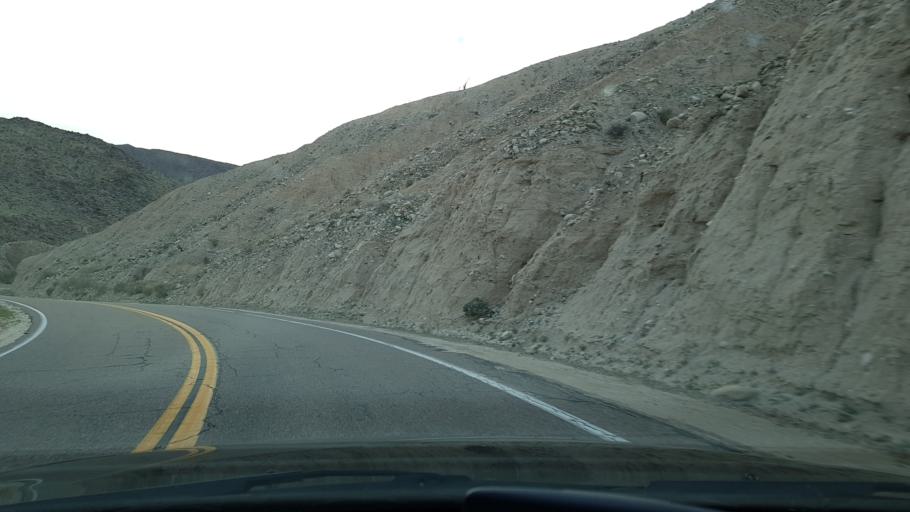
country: US
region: California
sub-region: San Diego County
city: Pine Valley
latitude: 32.8348
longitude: -116.1830
